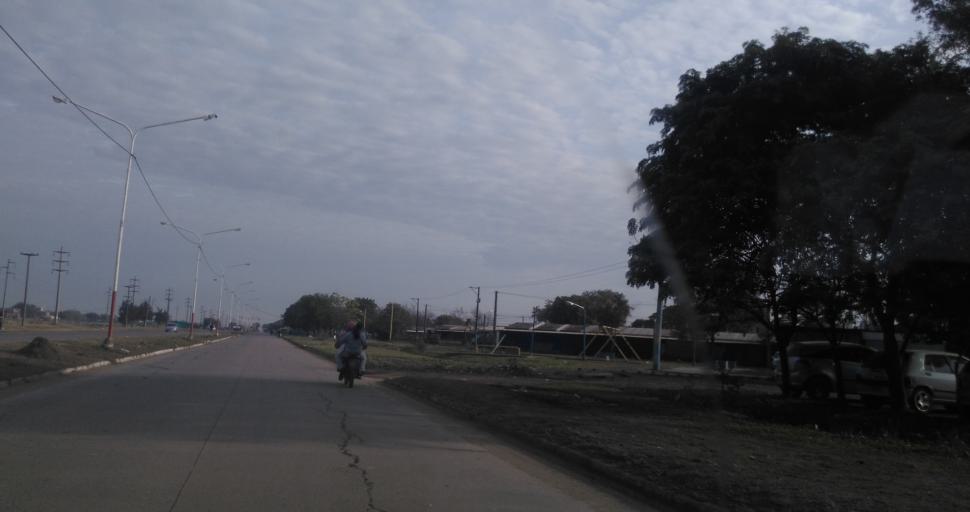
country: AR
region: Chaco
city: Resistencia
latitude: -27.4856
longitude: -58.9907
